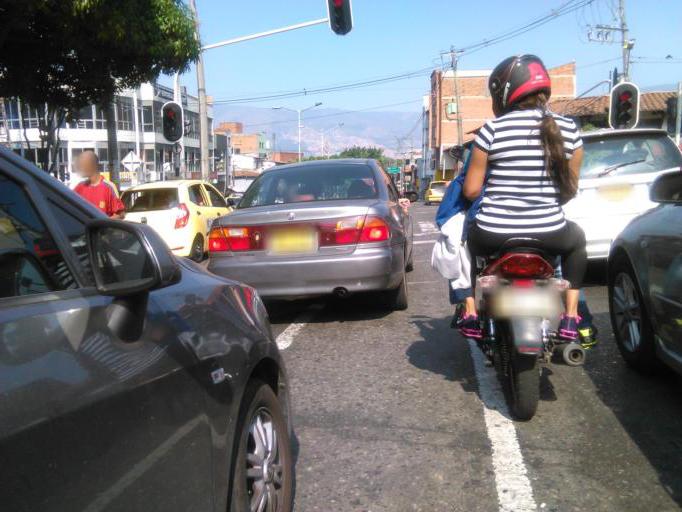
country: CO
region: Antioquia
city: Medellin
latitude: 6.2508
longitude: -75.6049
